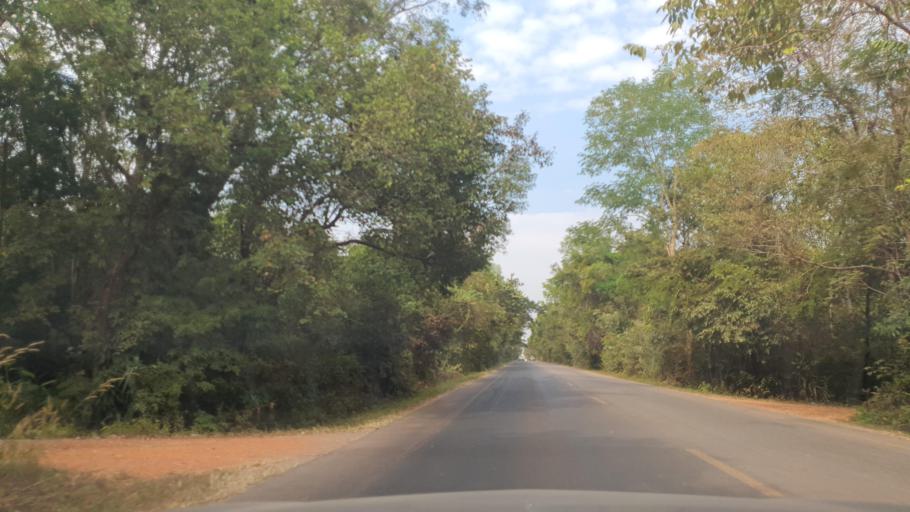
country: TH
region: Changwat Bueng Kan
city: Si Wilai
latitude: 18.2862
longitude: 103.8255
